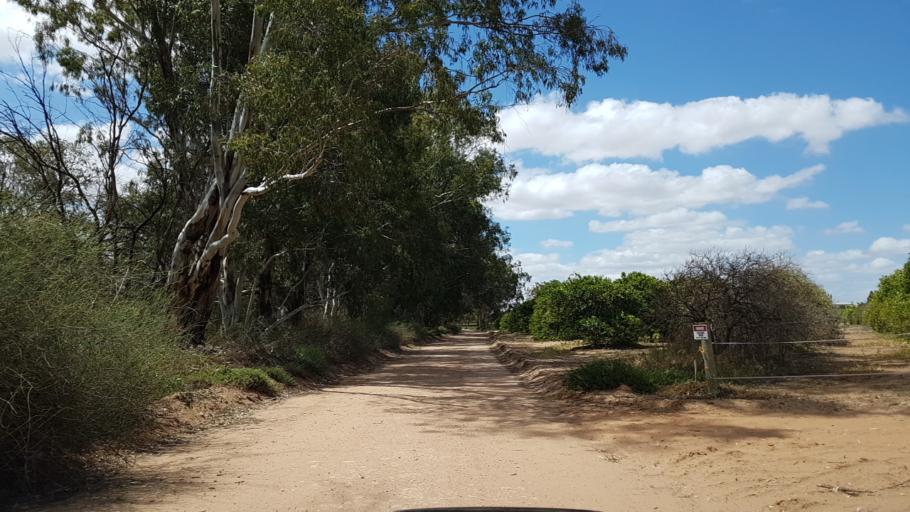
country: AU
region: South Australia
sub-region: Loxton Waikerie
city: Waikerie
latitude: -34.1750
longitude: 140.0219
